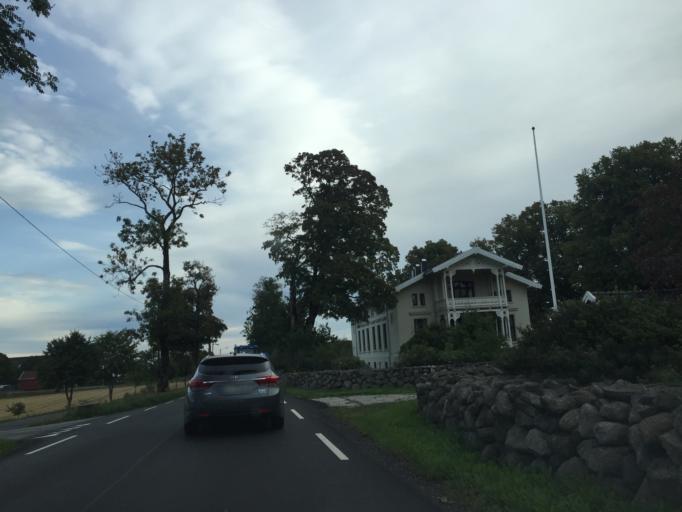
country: NO
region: Akershus
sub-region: As
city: As
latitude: 59.7153
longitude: 10.7745
